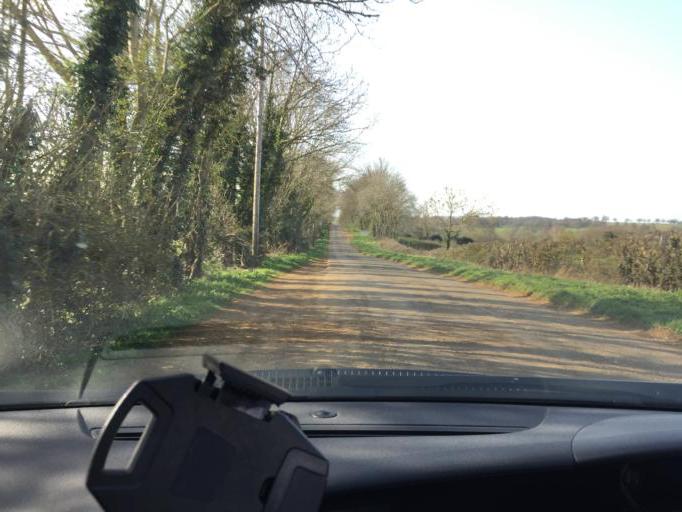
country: GB
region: England
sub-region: Oxfordshire
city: Bloxham
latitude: 52.0330
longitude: -1.3883
